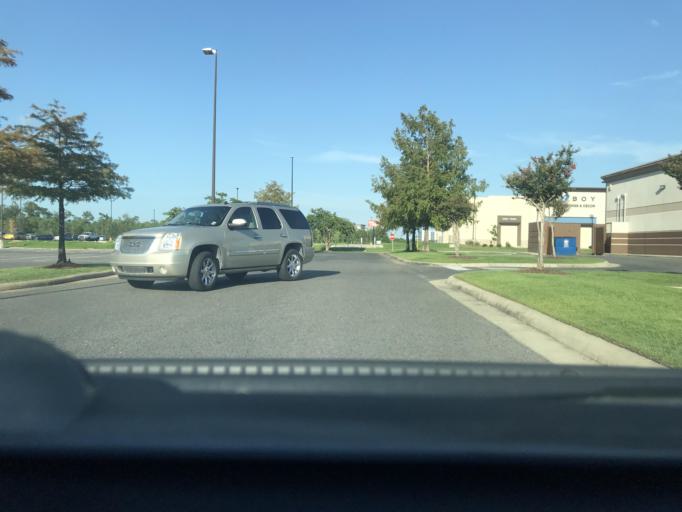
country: US
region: Louisiana
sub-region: Calcasieu Parish
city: Prien
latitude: 30.1986
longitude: -93.2463
